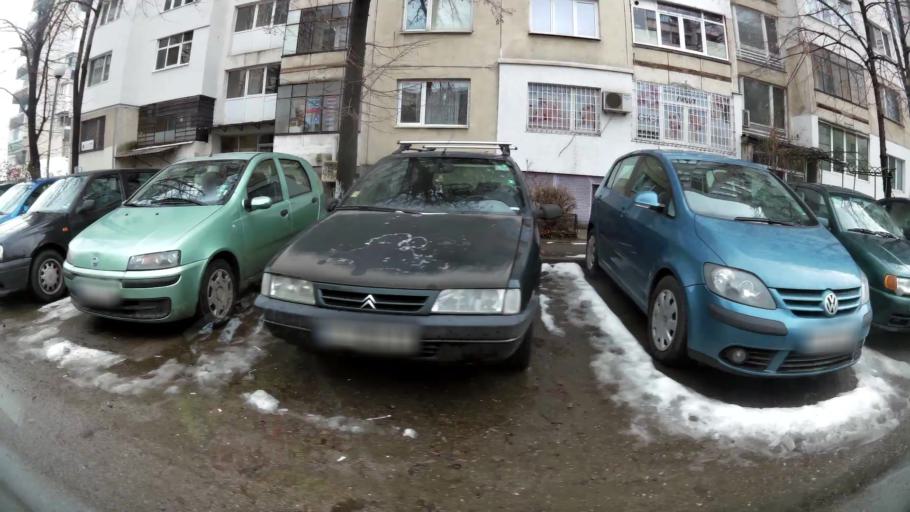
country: BG
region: Sofia-Capital
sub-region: Stolichna Obshtina
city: Sofia
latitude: 42.7140
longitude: 23.2620
